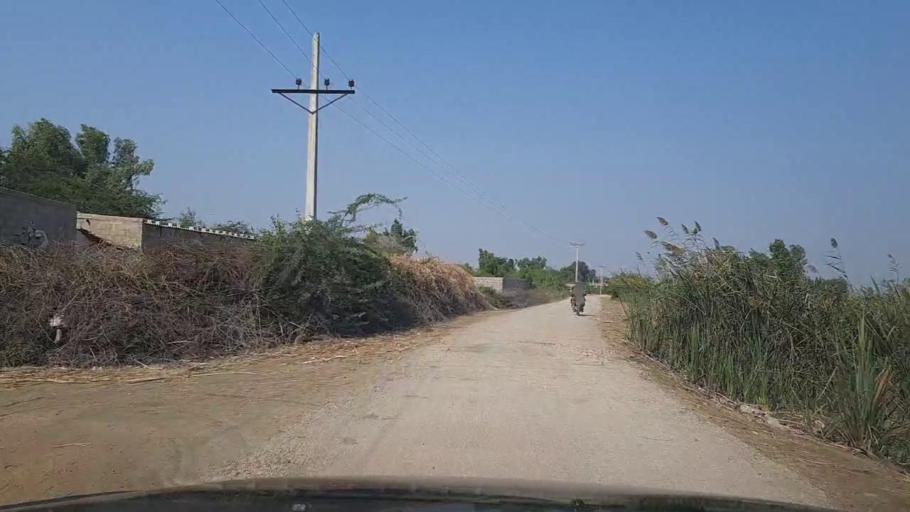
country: PK
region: Sindh
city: Thatta
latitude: 24.6131
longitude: 67.8211
